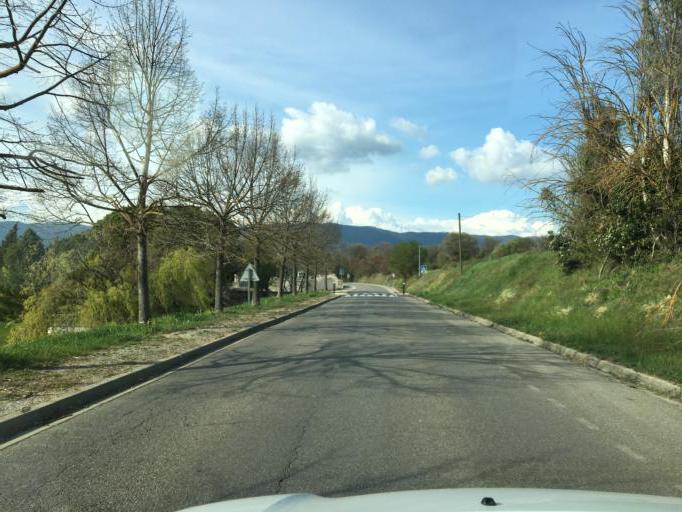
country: FR
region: Provence-Alpes-Cote d'Azur
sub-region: Departement du Vaucluse
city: Ansouis
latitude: 43.7411
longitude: 5.4641
